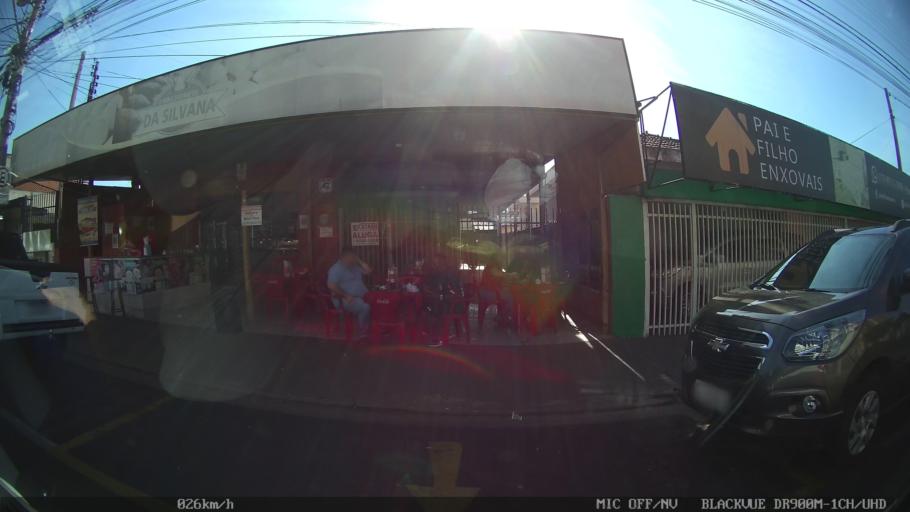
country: BR
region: Sao Paulo
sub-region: Sao Jose Do Rio Preto
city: Sao Jose do Rio Preto
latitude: -20.8038
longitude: -49.3903
